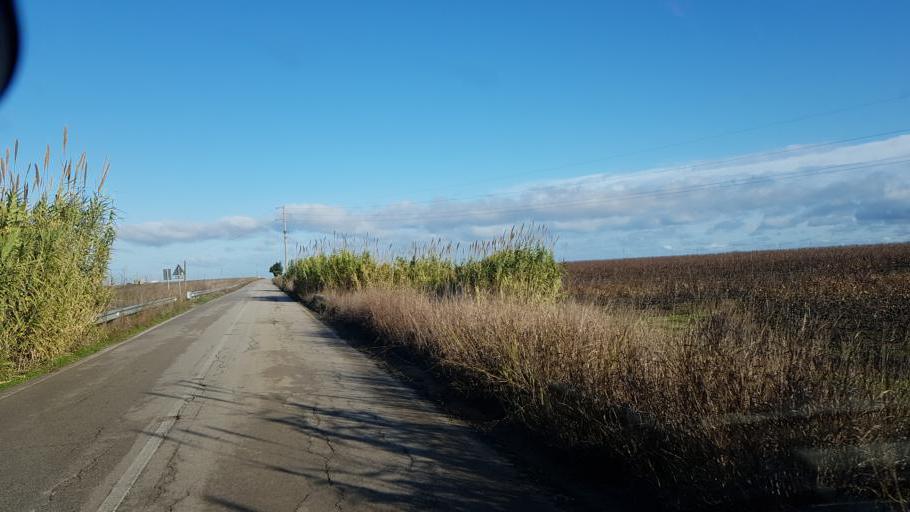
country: IT
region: Apulia
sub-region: Provincia di Brindisi
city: Tuturano
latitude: 40.5695
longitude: 17.9493
